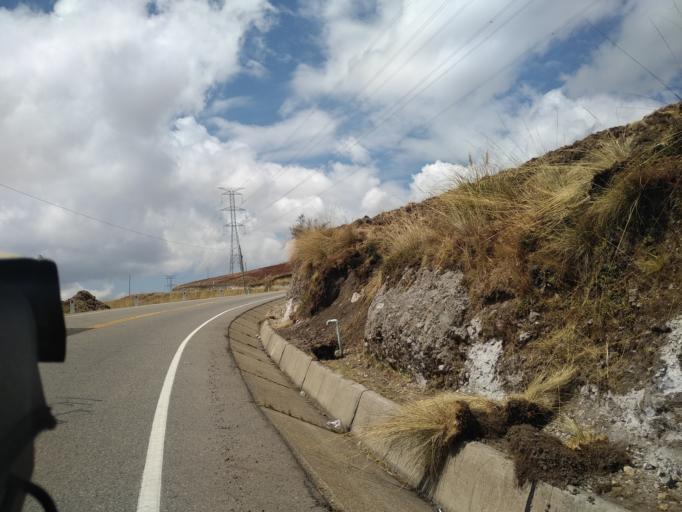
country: PE
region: La Libertad
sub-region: Provincia de Santiago de Chuco
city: Quiruvilca
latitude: -7.9225
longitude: -78.1530
